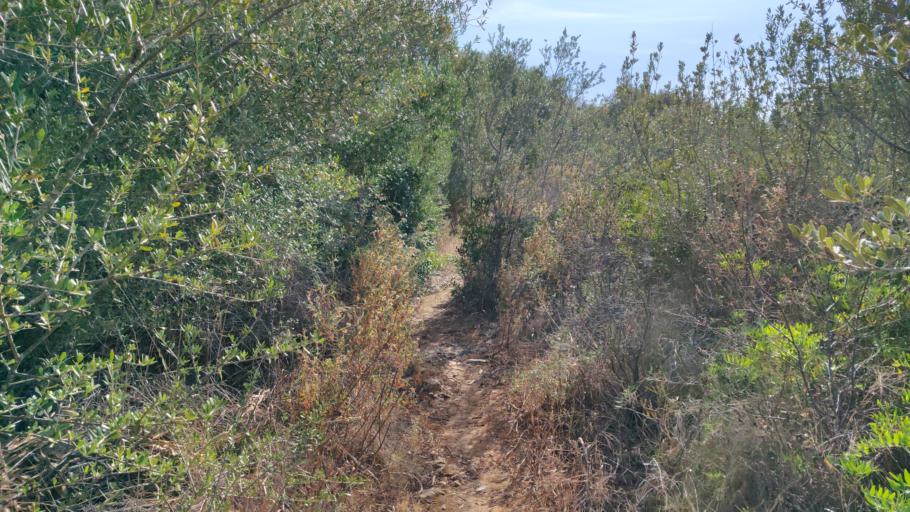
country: ES
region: Balearic Islands
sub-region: Illes Balears
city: Felanitx
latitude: 39.4530
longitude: 3.2616
